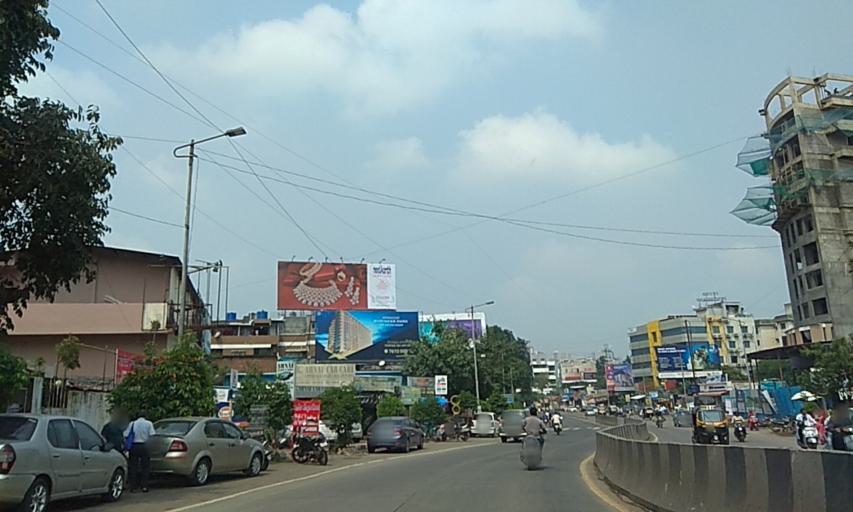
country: IN
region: Maharashtra
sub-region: Pune Division
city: Khadki
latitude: 18.5596
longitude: 73.7900
